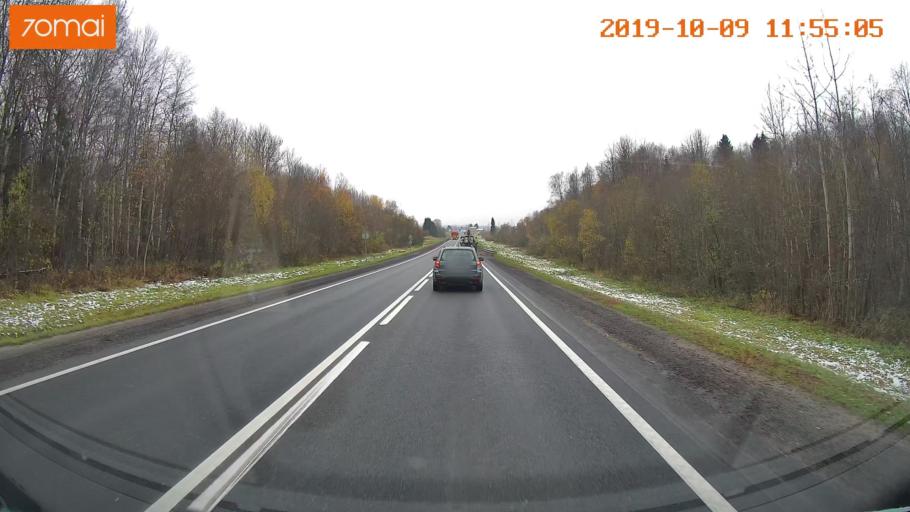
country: RU
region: Vologda
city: Gryazovets
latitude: 58.7516
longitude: 40.2845
